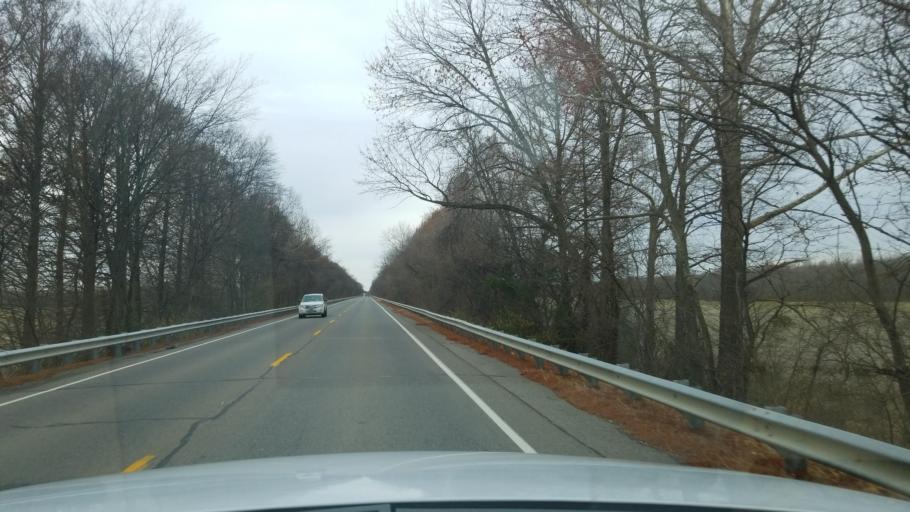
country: US
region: Indiana
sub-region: Posey County
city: Mount Vernon
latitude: 37.9290
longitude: -87.9660
